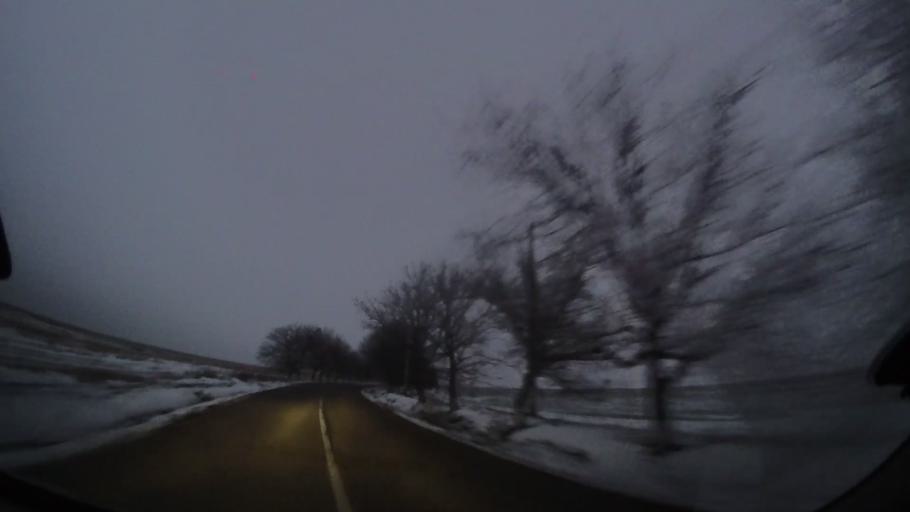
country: RO
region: Vaslui
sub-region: Comuna Dimitrie Cantemir
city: Dimitrie Cantemir
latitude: 46.5139
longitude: 28.0319
